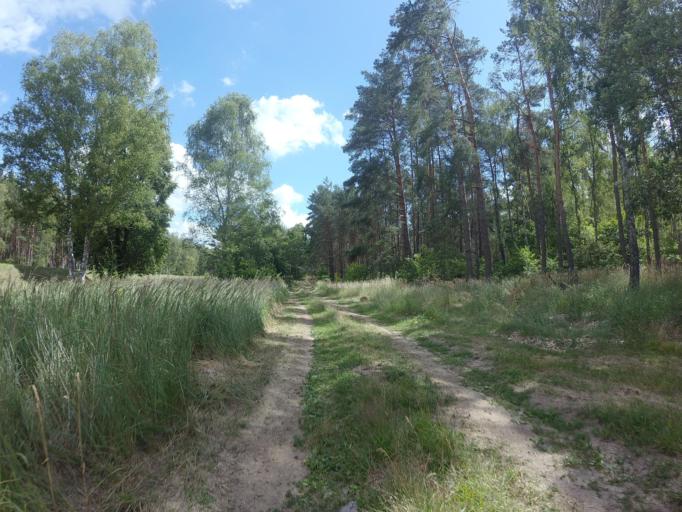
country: PL
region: West Pomeranian Voivodeship
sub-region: Powiat choszczenski
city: Drawno
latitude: 53.2827
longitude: 15.6946
